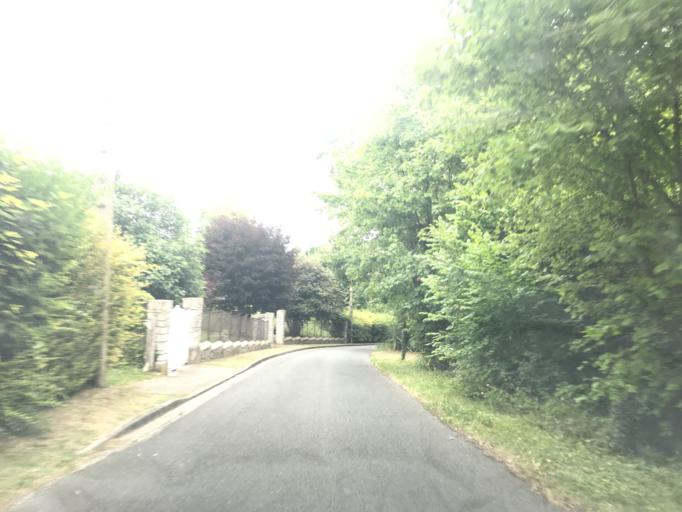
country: FR
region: Haute-Normandie
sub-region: Departement de l'Eure
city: Vernon
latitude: 49.0807
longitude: 1.4594
